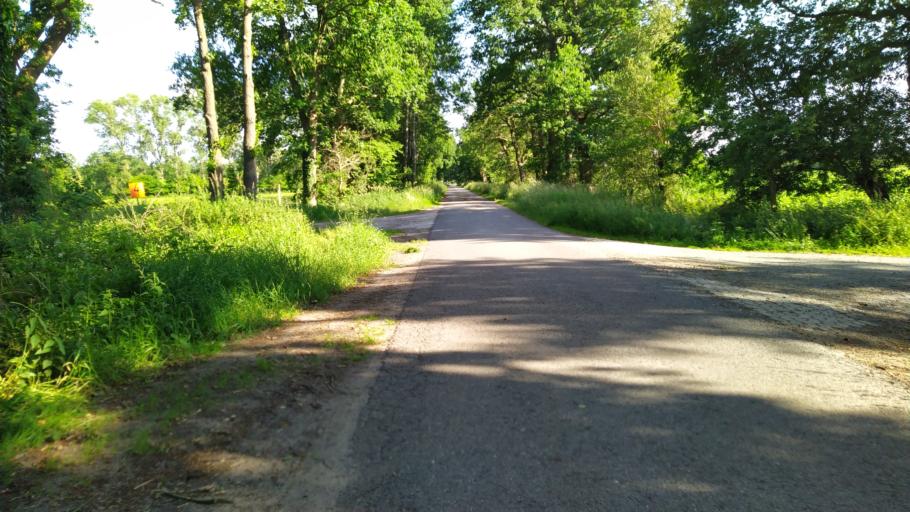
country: DE
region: Lower Saxony
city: Lintig
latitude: 53.6101
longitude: 8.8898
